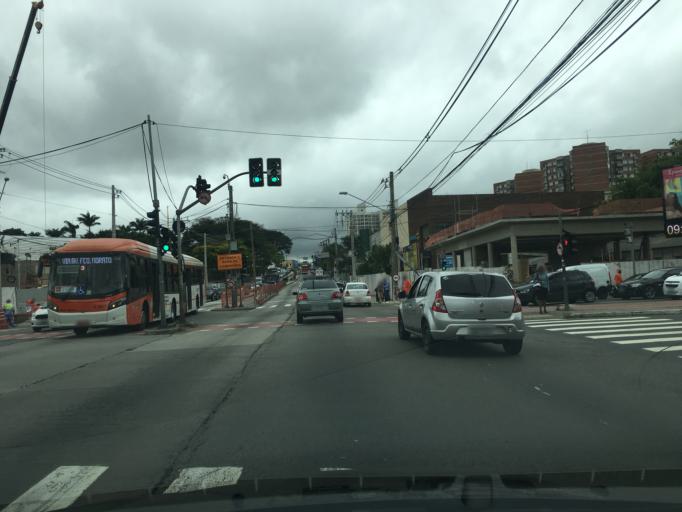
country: BR
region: Sao Paulo
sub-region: Taboao Da Serra
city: Taboao da Serra
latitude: -23.5867
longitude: -46.7247
